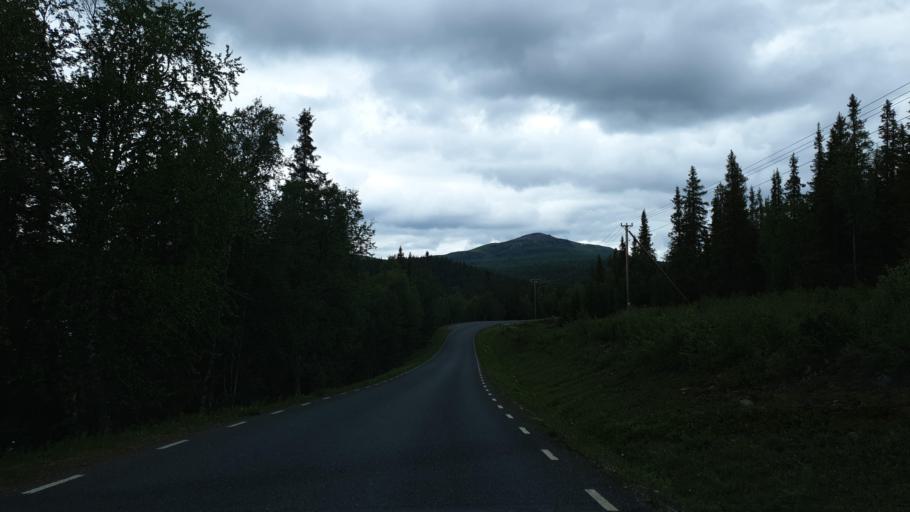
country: SE
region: Vaesterbotten
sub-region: Vilhelmina Kommun
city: Sjoberg
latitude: 65.2688
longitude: 15.3696
